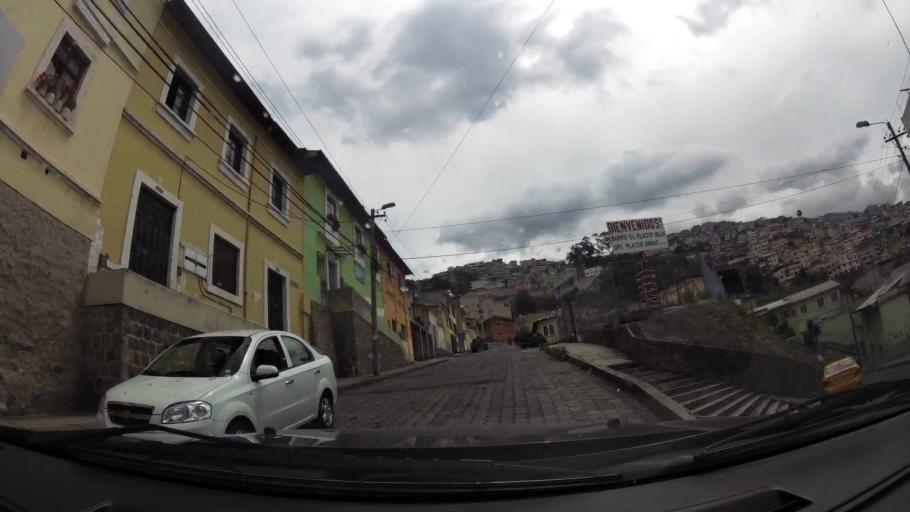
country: EC
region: Pichincha
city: Quito
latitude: -0.2160
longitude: -78.5189
